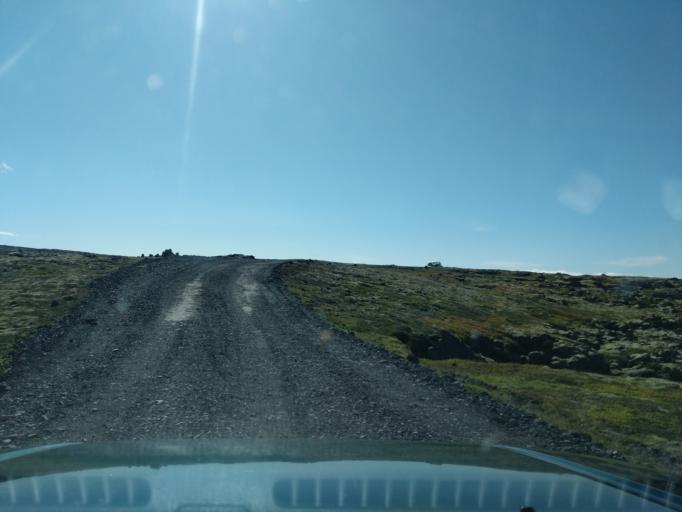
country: IS
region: West
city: Olafsvik
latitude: 64.8743
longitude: -24.0166
